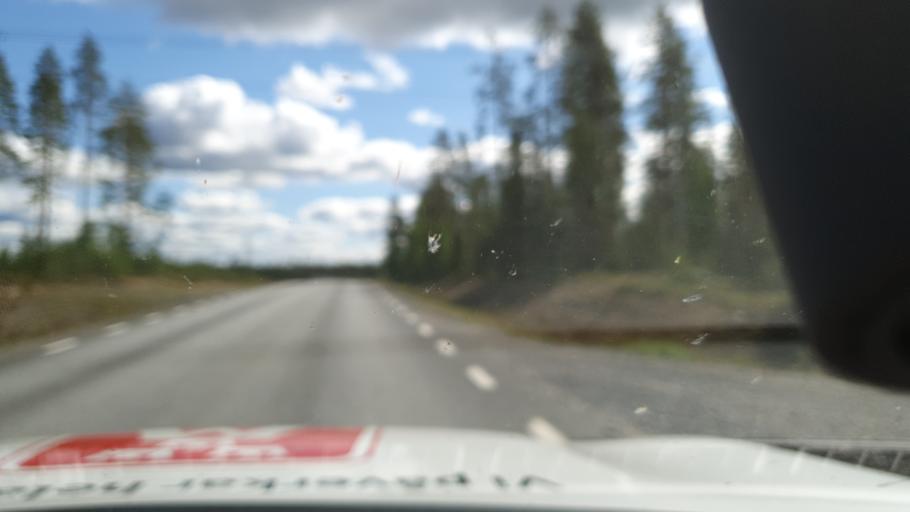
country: SE
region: Vaesterbotten
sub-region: Mala Kommun
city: Mala
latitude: 65.1479
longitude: 18.7475
